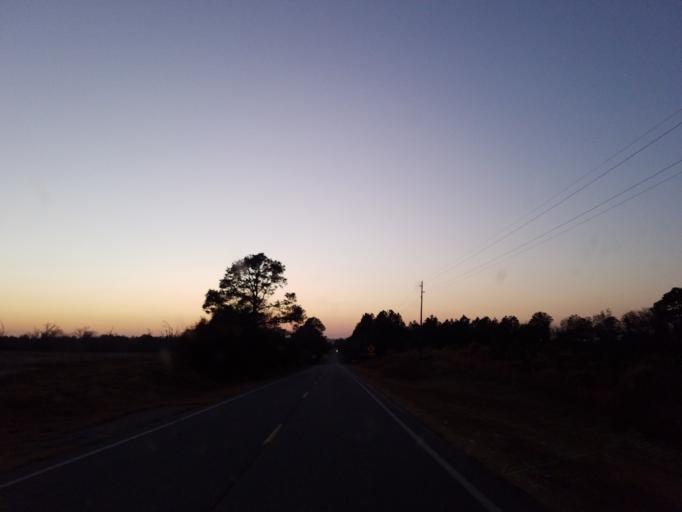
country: US
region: Georgia
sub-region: Turner County
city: Ashburn
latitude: 31.8596
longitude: -83.6102
